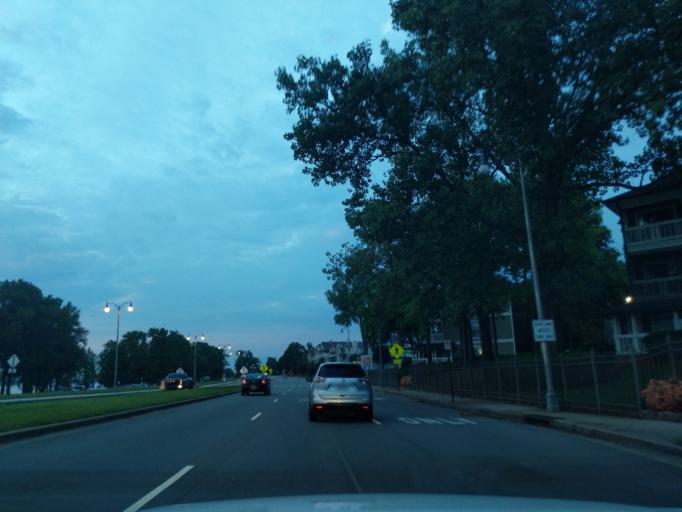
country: US
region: Tennessee
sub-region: Shelby County
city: Memphis
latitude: 35.1600
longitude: -90.0559
